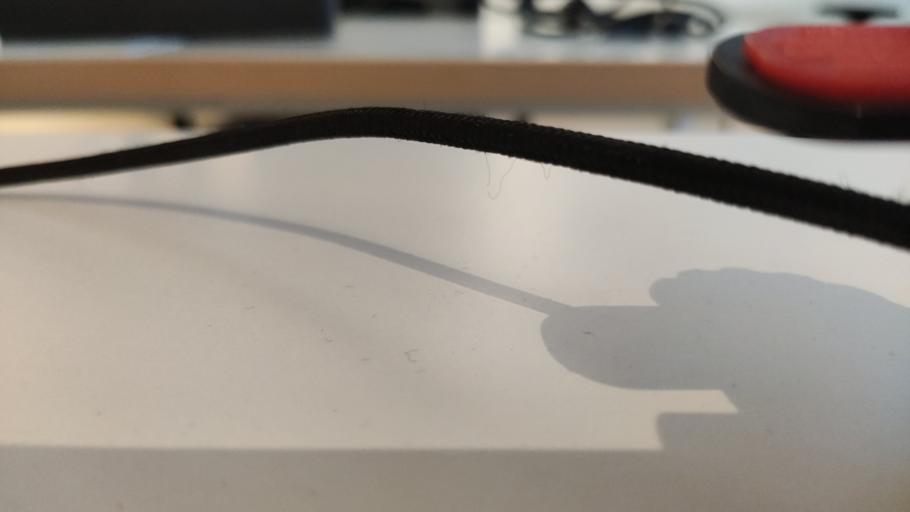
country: RU
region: Moskovskaya
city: Sychevo
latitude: 55.8413
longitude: 36.3357
